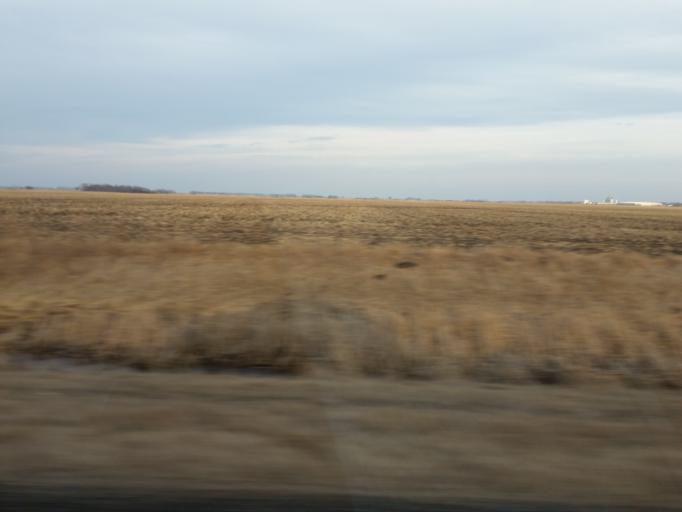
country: US
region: North Dakota
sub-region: Traill County
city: Hillsboro
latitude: 47.3295
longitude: -97.2176
